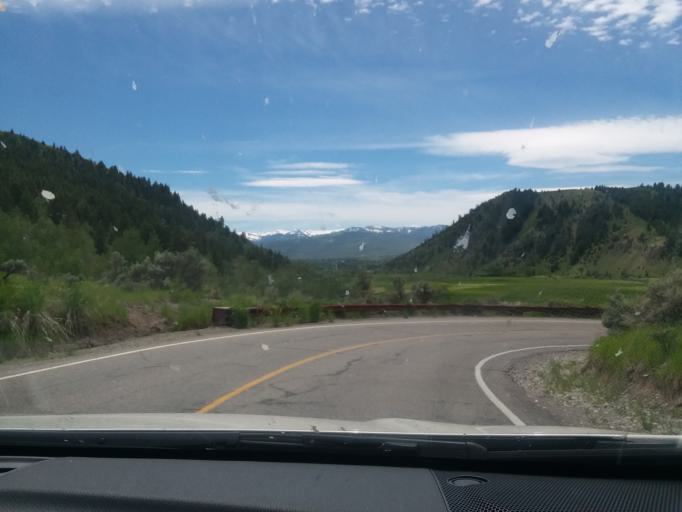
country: US
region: Wyoming
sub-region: Teton County
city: Jackson
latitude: 43.4927
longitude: -110.7859
